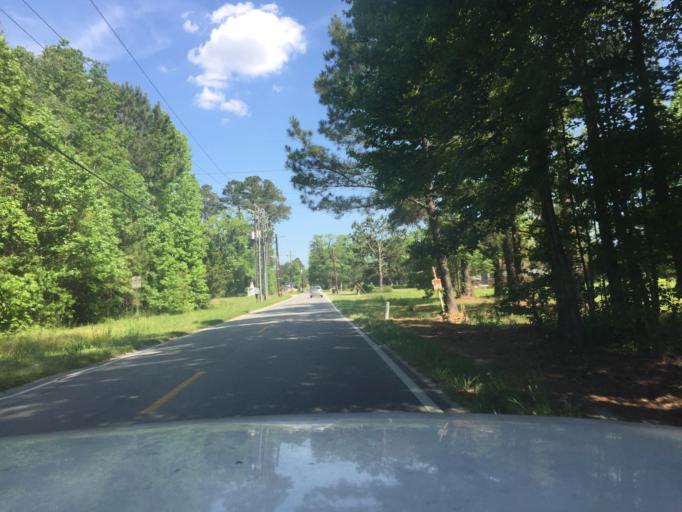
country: US
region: Georgia
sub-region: Chatham County
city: Georgetown
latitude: 32.0003
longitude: -81.2766
